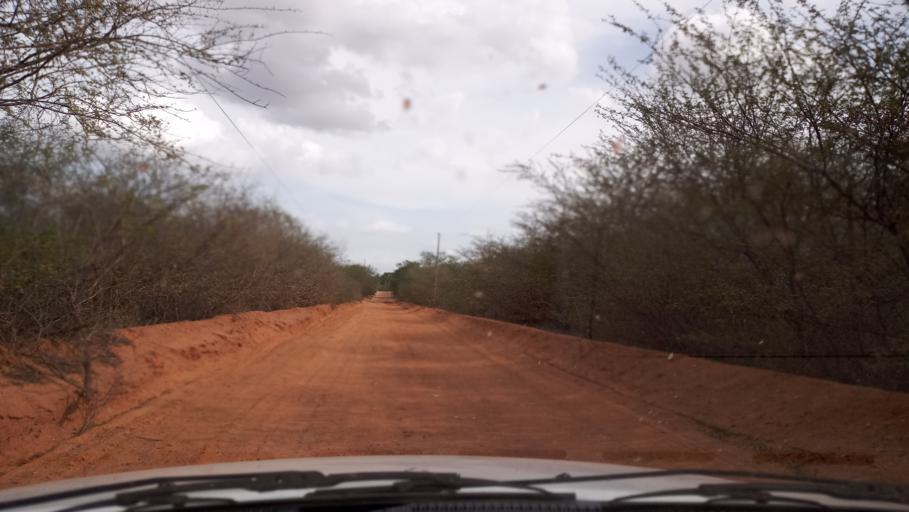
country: BR
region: Rio Grande do Norte
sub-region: Joao Camara
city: Joao Camara
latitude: -5.5017
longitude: -35.8251
